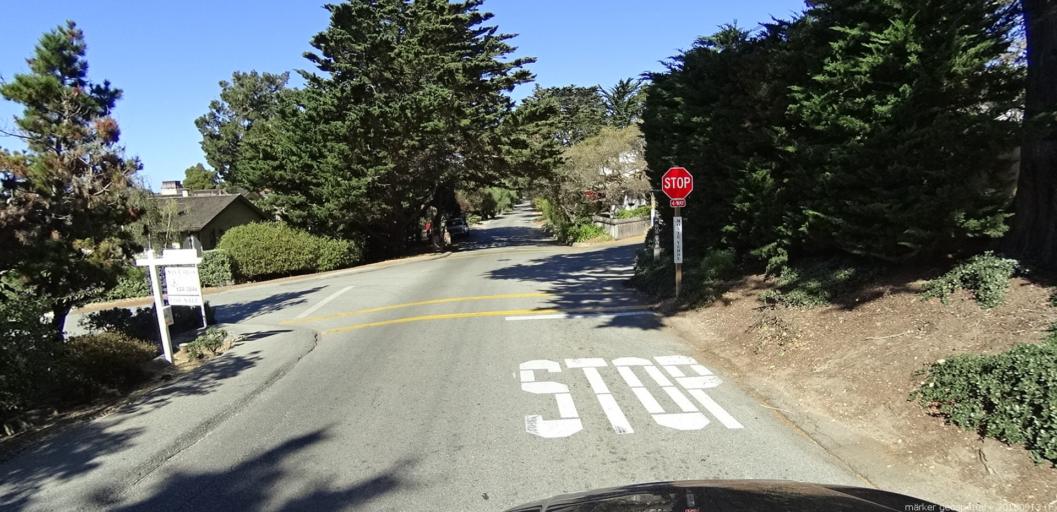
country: US
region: California
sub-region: Monterey County
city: Carmel-by-the-Sea
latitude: 36.5445
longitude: -121.9241
